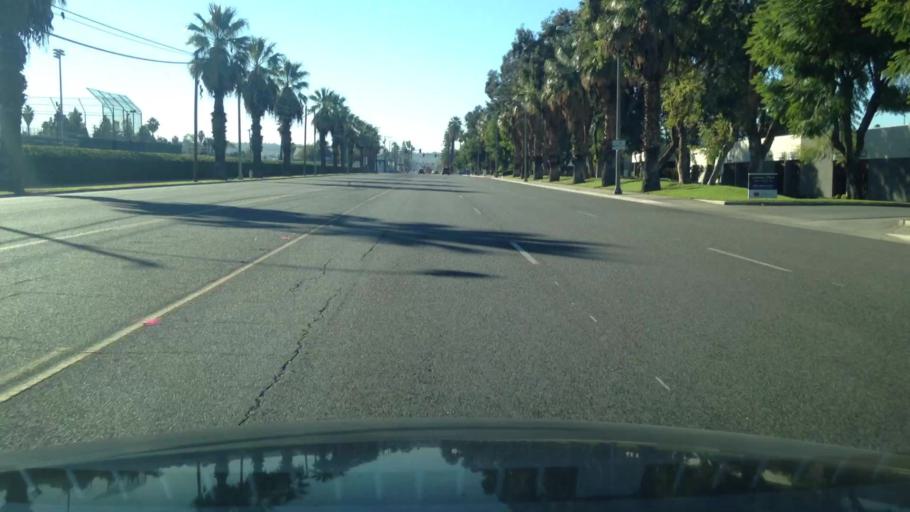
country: US
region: California
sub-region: Riverside County
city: Highgrove
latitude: 33.9823
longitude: -117.3485
